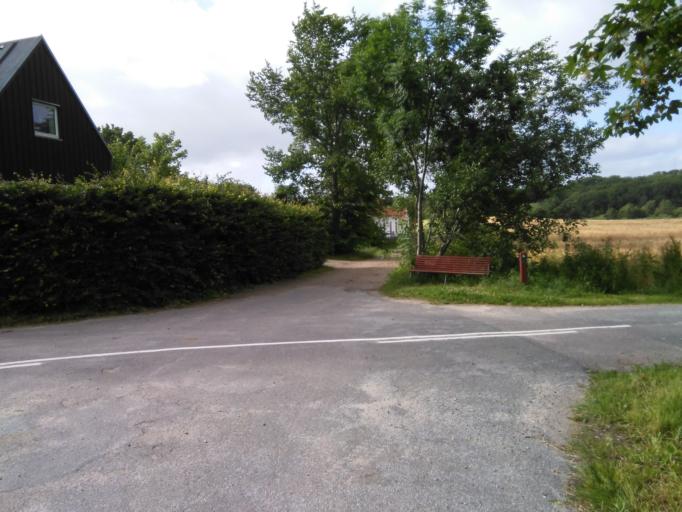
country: DK
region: Central Jutland
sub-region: Arhus Kommune
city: Beder
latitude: 56.0758
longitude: 10.2001
